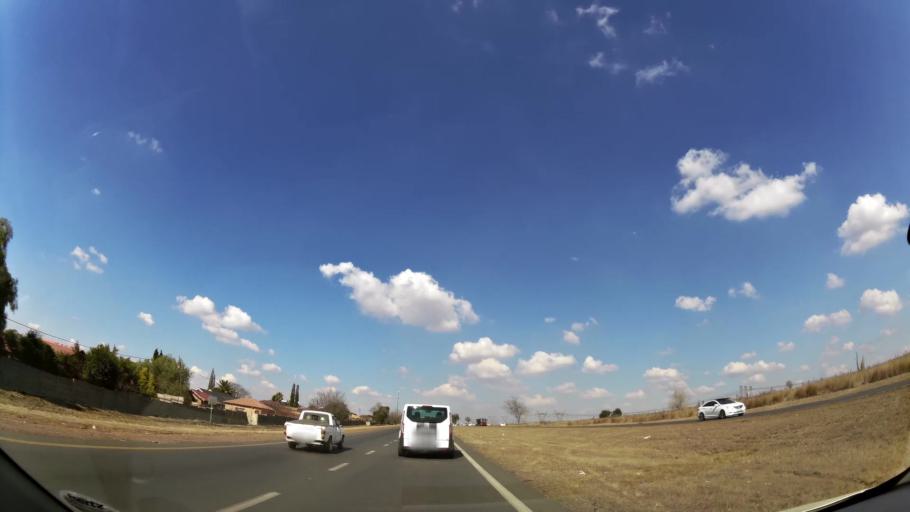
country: ZA
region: Mpumalanga
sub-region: Nkangala District Municipality
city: Witbank
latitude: -25.9359
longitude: 29.2388
